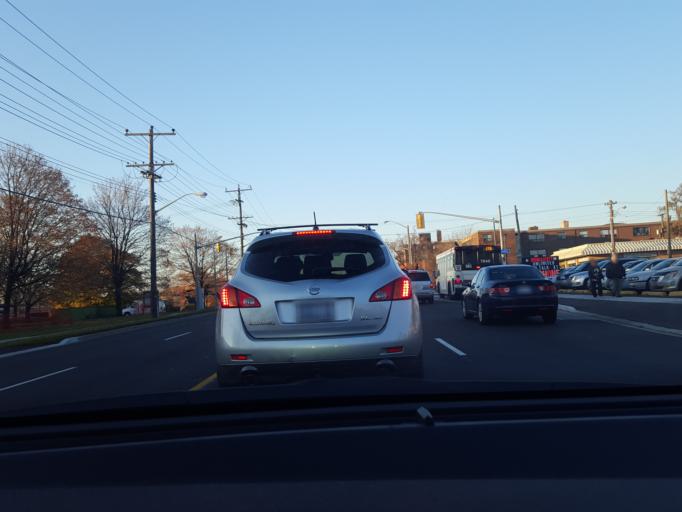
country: CA
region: Ontario
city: Scarborough
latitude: 43.7584
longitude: -79.2893
